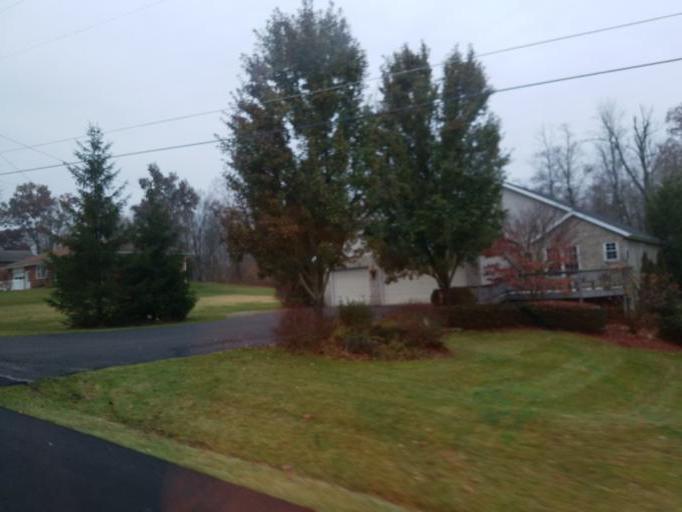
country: US
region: Ohio
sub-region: Richland County
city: Lexington
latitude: 40.6978
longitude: -82.5299
